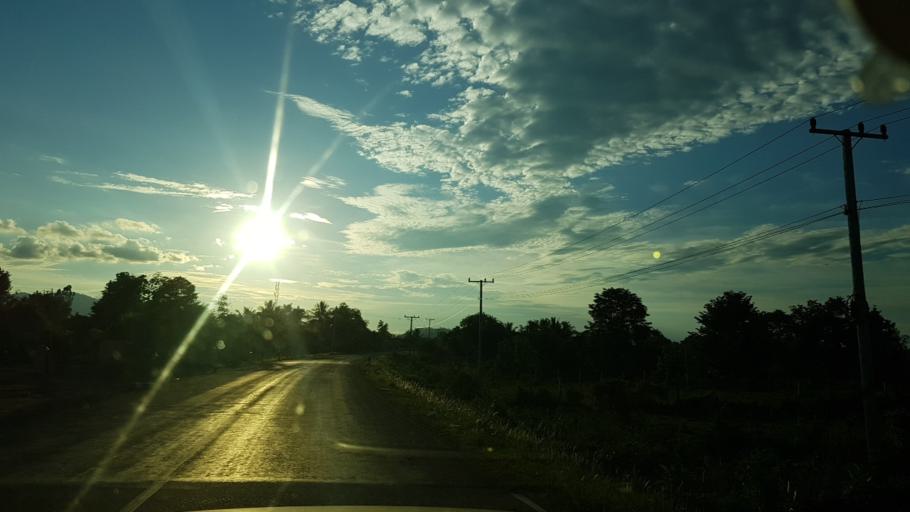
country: TH
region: Nong Khai
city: Sangkhom
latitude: 18.0920
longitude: 102.2894
